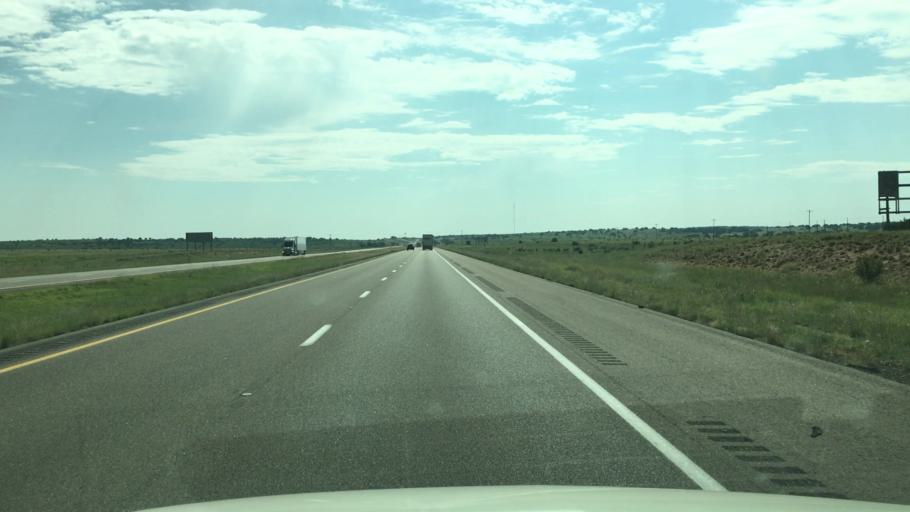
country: US
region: New Mexico
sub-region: Guadalupe County
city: Santa Rosa
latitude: 34.9891
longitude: -105.2475
